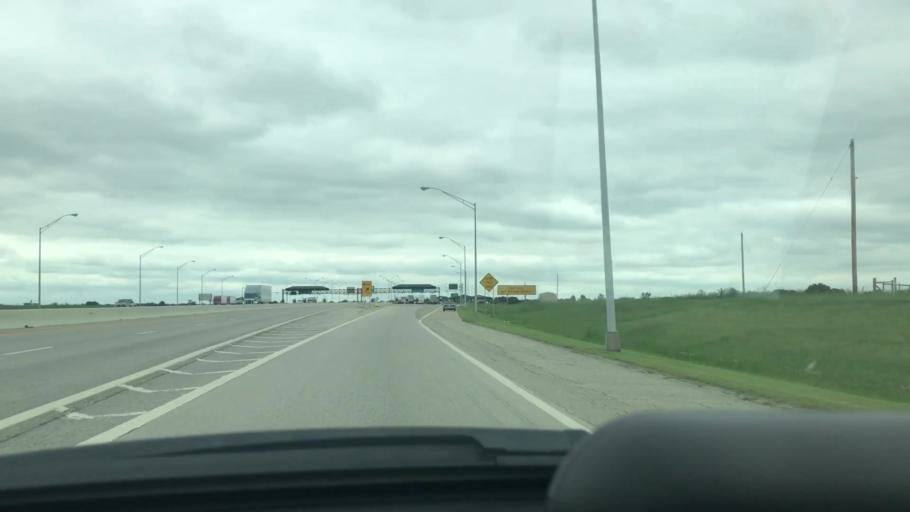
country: US
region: Oklahoma
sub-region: Craig County
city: Vinita
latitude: 36.6014
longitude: -95.1898
